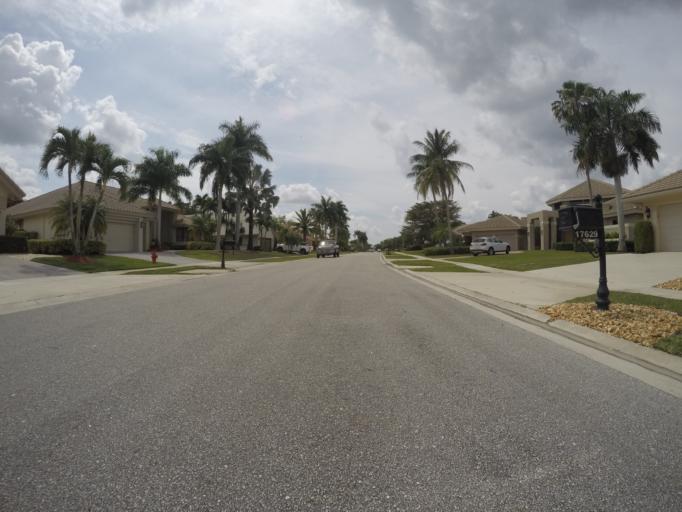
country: US
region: Florida
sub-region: Palm Beach County
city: Villages of Oriole
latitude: 26.4138
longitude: -80.2152
